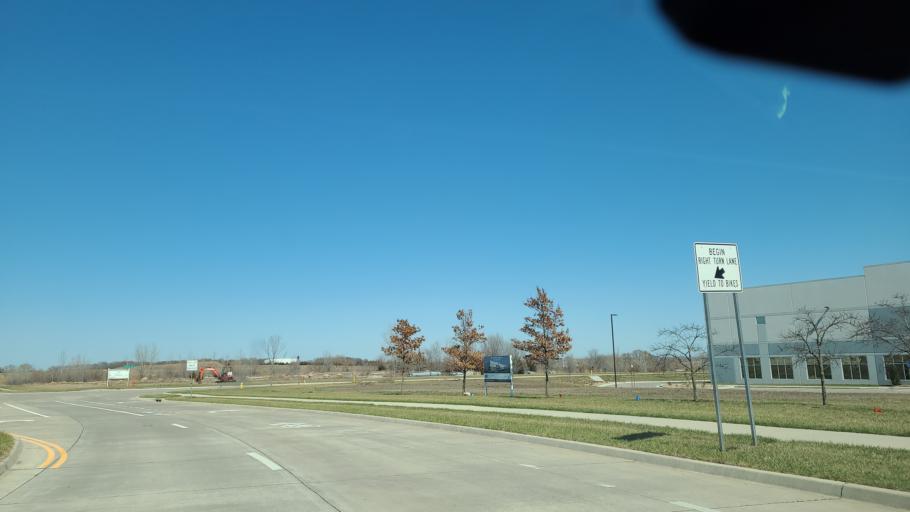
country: US
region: Kansas
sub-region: Douglas County
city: Lawrence
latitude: 38.9446
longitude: -95.2039
